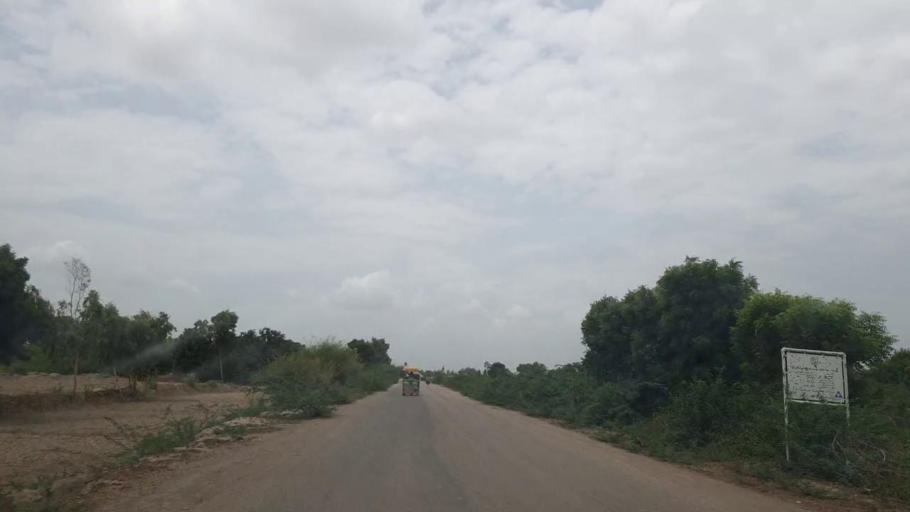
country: PK
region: Sindh
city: Naukot
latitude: 24.8861
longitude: 69.2502
